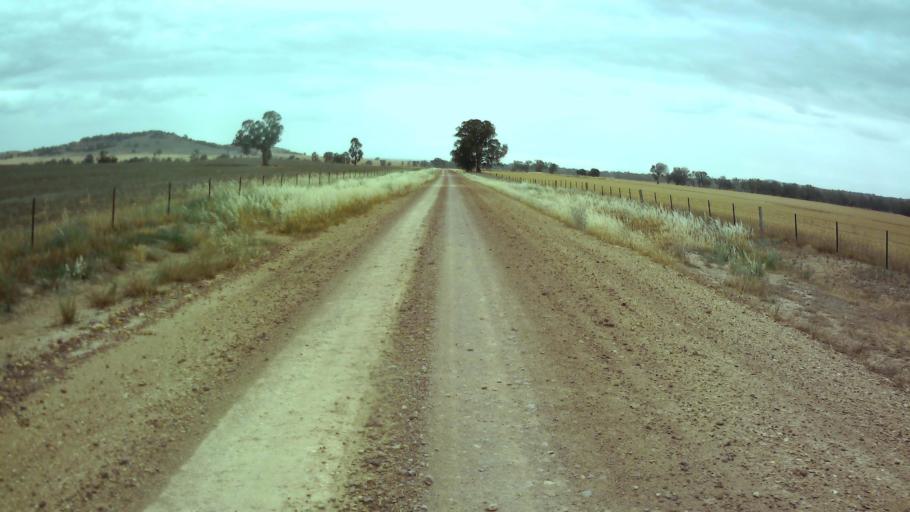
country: AU
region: New South Wales
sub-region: Weddin
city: Grenfell
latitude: -33.9240
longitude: 148.2829
